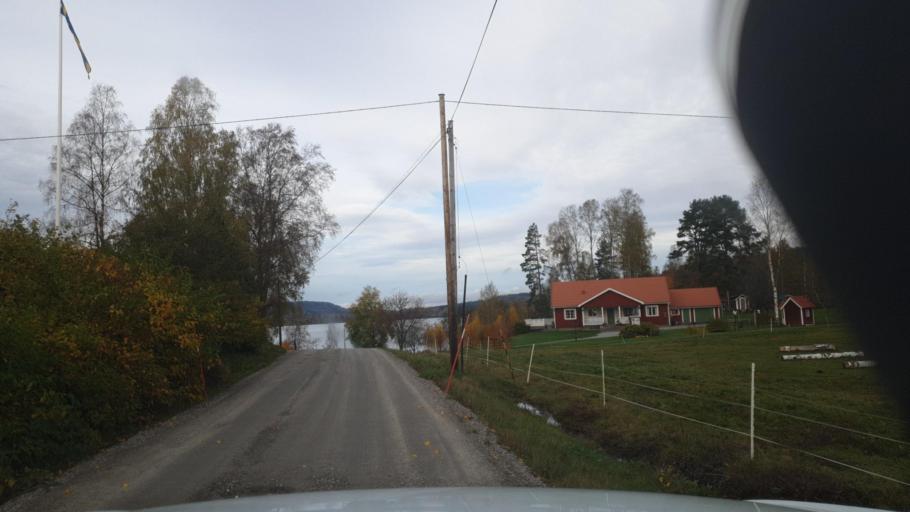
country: SE
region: Vaermland
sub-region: Arvika Kommun
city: Arvika
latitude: 59.7190
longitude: 12.8389
